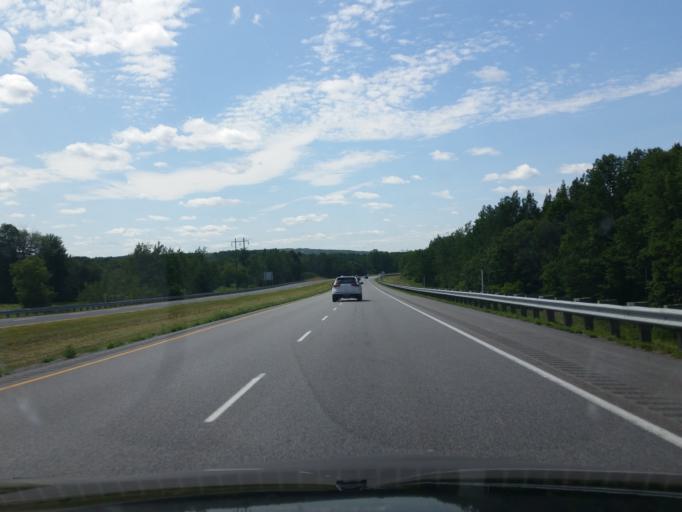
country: CA
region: Quebec
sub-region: Monteregie
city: Hudson
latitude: 45.4377
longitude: -74.1842
